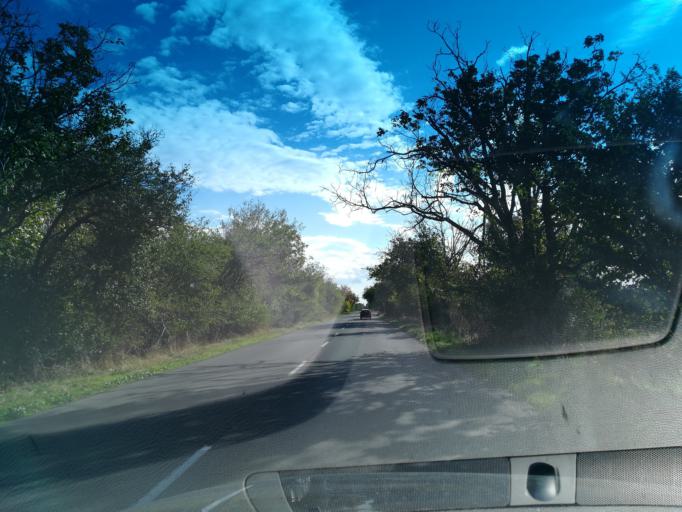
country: BG
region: Stara Zagora
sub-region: Obshtina Stara Zagora
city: Stara Zagora
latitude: 42.3705
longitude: 25.6532
